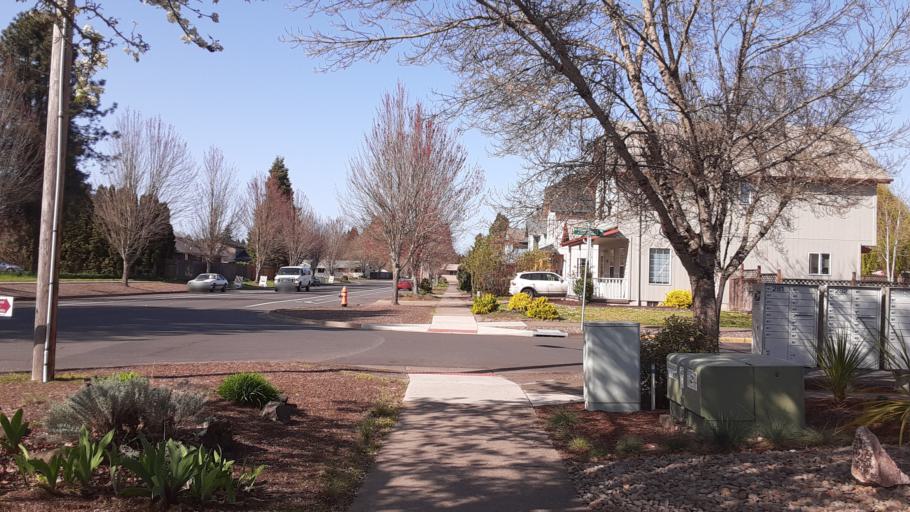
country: US
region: Oregon
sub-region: Benton County
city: Corvallis
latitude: 44.5355
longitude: -123.2565
